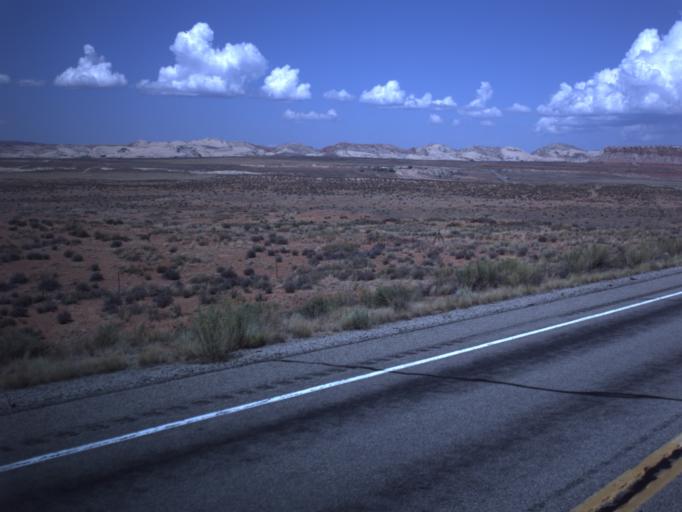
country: US
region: Utah
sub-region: San Juan County
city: Blanding
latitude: 37.2435
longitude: -109.6075
